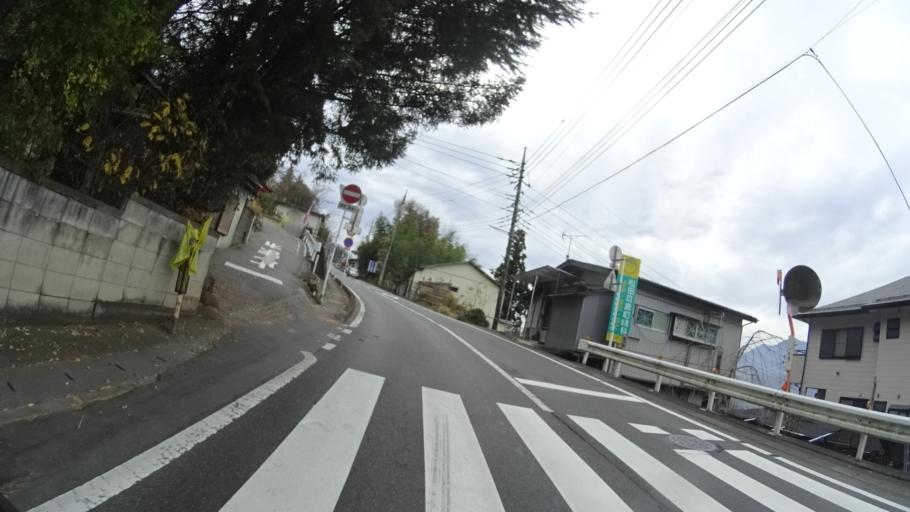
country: JP
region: Gunma
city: Numata
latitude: 36.6480
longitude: 139.0373
